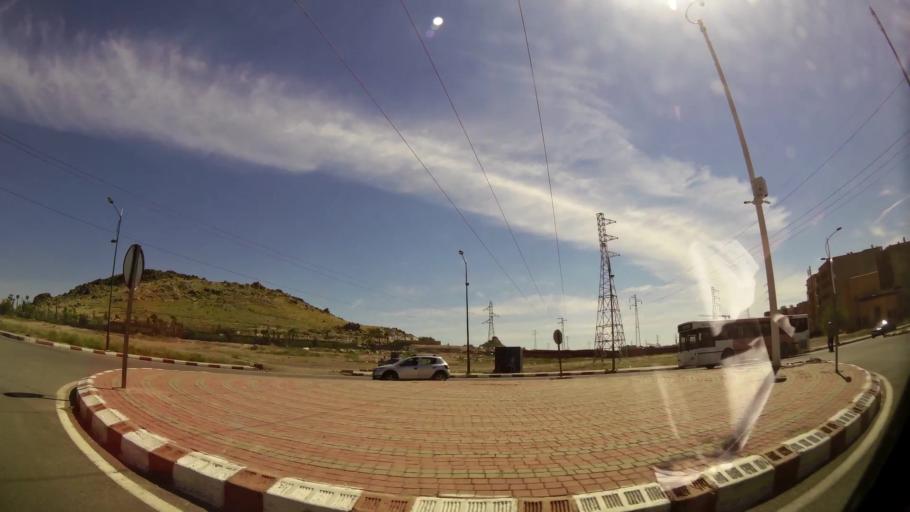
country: MA
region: Marrakech-Tensift-Al Haouz
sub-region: Marrakech
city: Marrakesh
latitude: 31.6725
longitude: -8.0164
